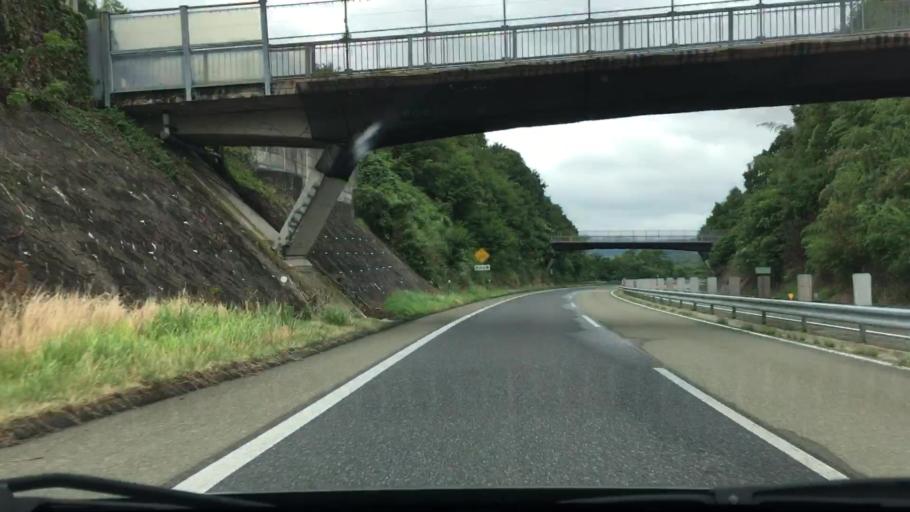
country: JP
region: Hiroshima
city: Shobara
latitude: 34.8299
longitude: 133.0480
